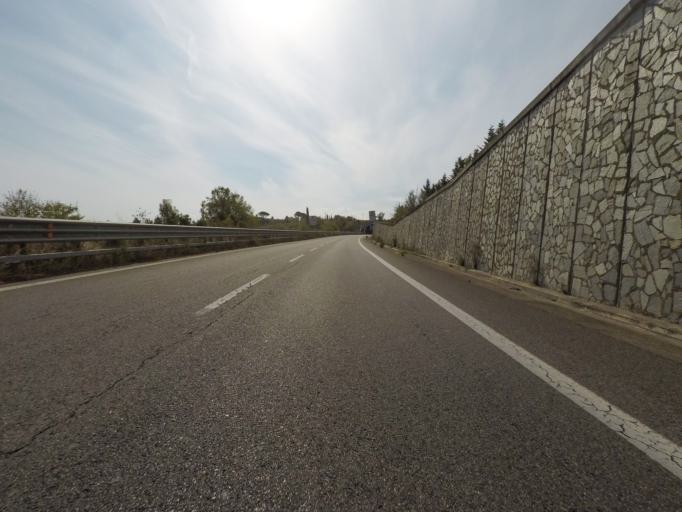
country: IT
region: Tuscany
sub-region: Provincia di Siena
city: Siena
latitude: 43.2763
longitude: 11.3332
